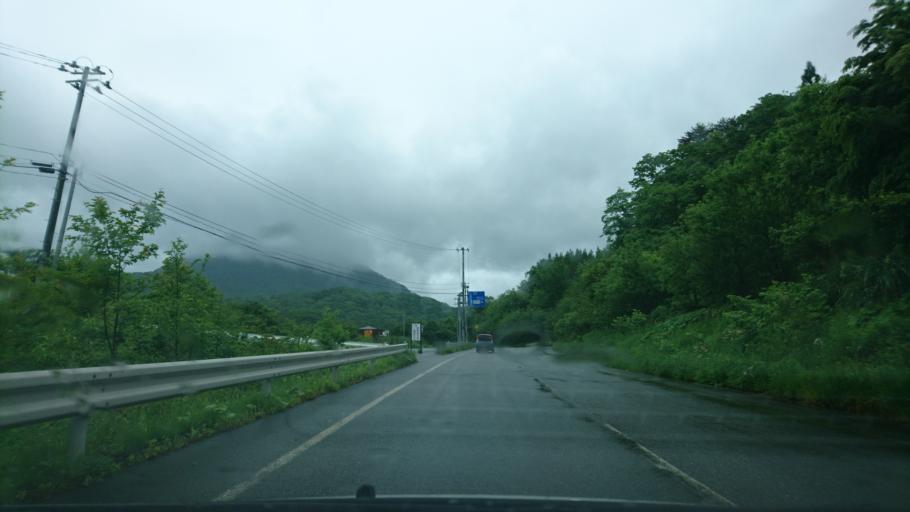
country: JP
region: Iwate
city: Ichinoseki
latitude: 39.0156
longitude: 140.8804
